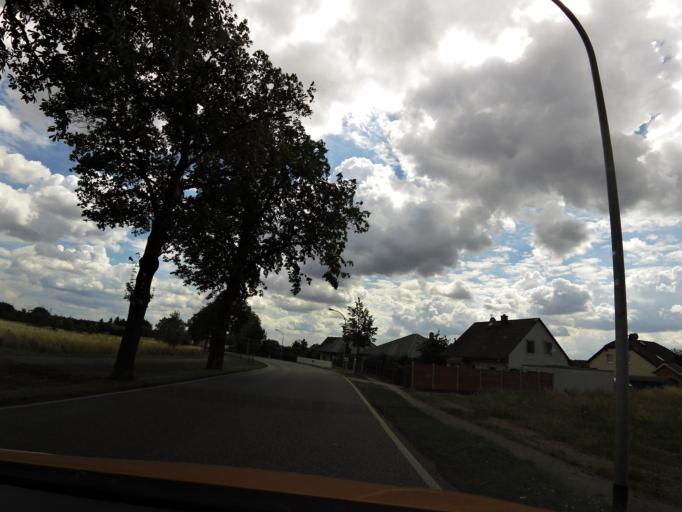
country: DE
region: Brandenburg
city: Grossbeeren
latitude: 52.3422
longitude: 13.3580
